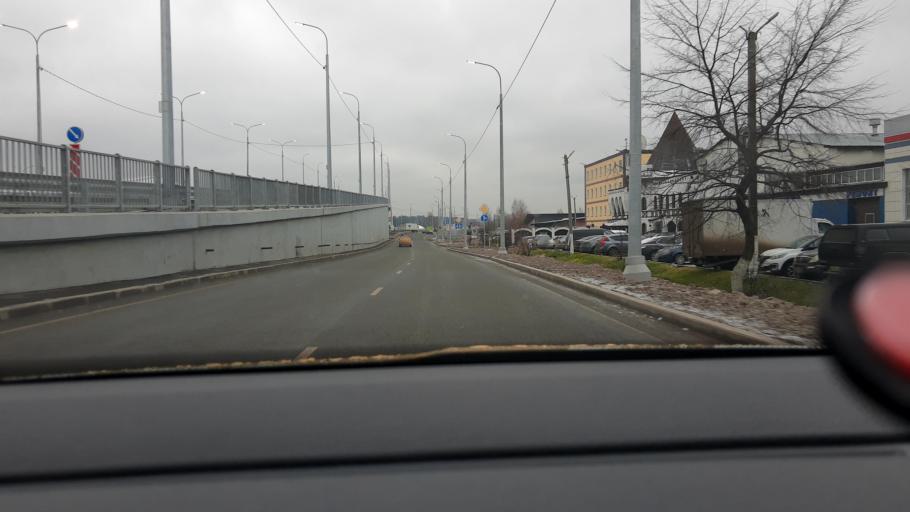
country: RU
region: Moskovskaya
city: Lesnyye Polyany
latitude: 55.9817
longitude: 37.8632
